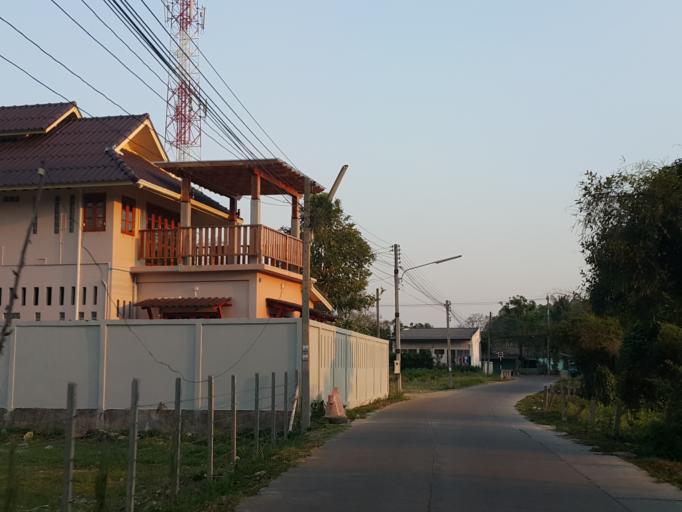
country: TH
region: Chiang Mai
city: San Sai
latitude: 18.8795
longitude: 98.9671
